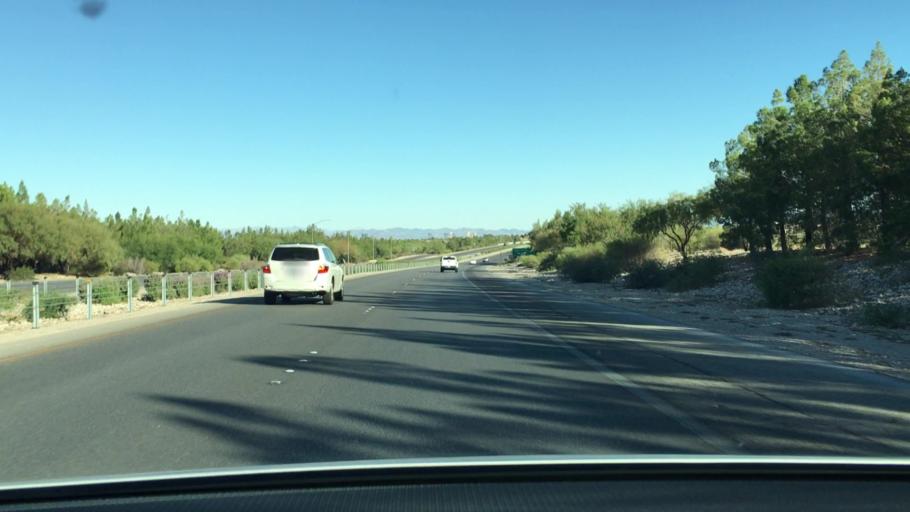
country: US
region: Nevada
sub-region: Clark County
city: Summerlin South
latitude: 36.1913
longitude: -115.3142
